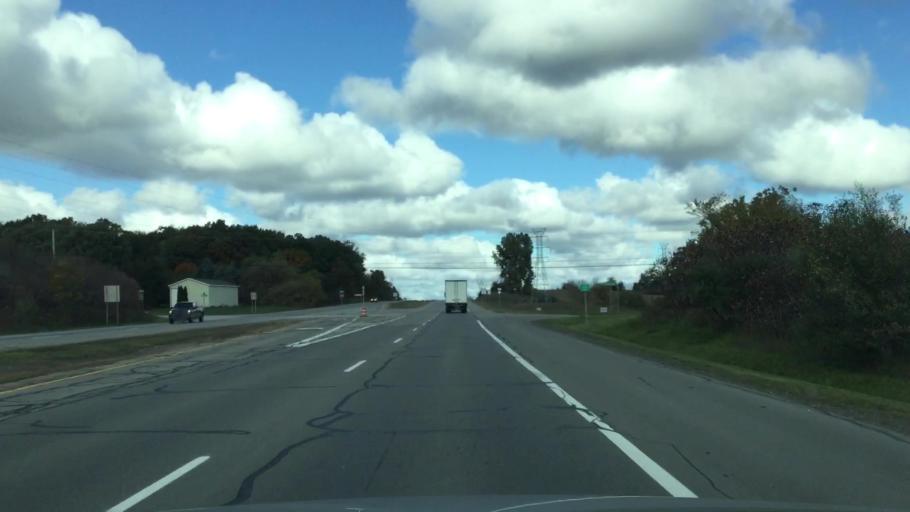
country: US
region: Michigan
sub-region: Oakland County
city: Oxford
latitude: 42.8826
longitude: -83.3046
